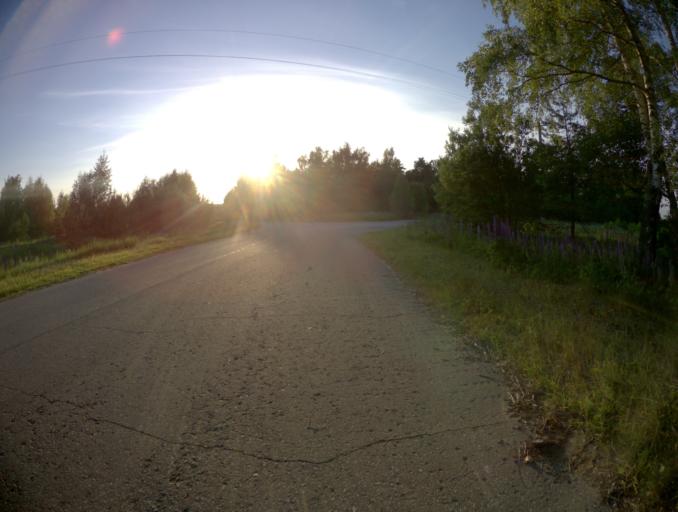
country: RU
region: Vladimir
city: Golovino
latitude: 55.9867
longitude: 40.5206
